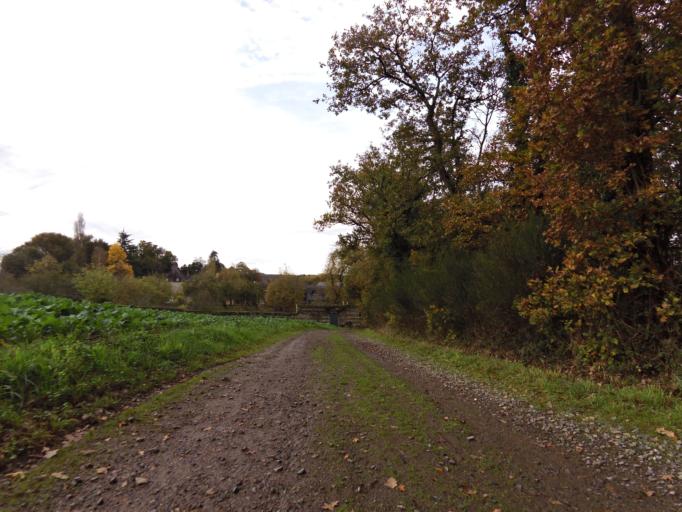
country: FR
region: Brittany
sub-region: Departement d'Ille-et-Vilaine
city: Bourg-des-Comptes
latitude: 47.9350
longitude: -1.7541
